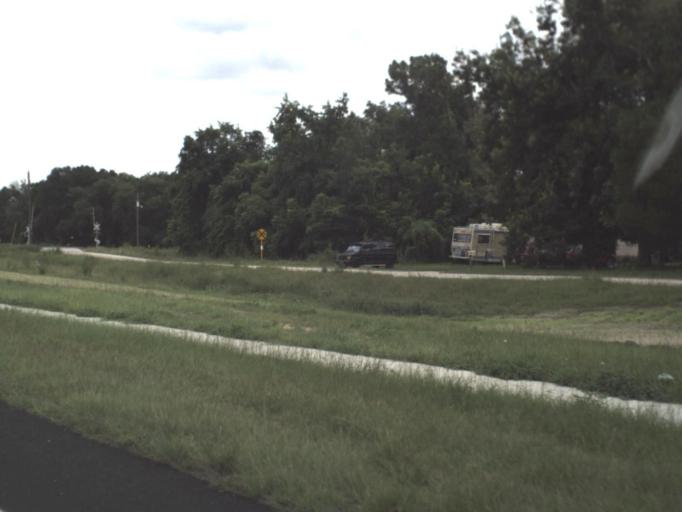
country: US
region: Florida
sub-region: Pasco County
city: Lacoochee
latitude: 28.4413
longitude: -82.1897
